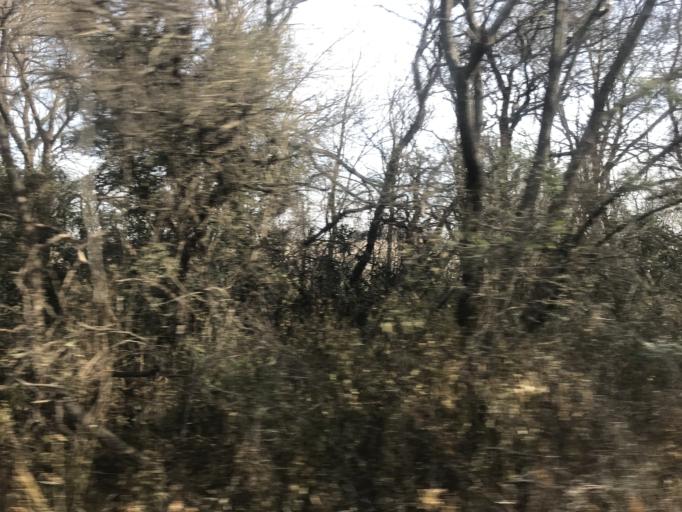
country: AR
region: Cordoba
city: Laguna Larga
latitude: -31.8080
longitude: -63.7759
